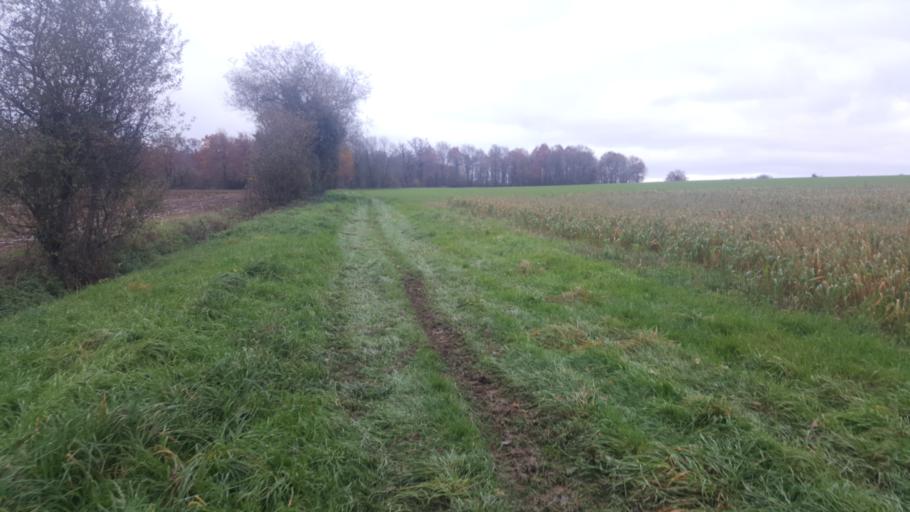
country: FR
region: Poitou-Charentes
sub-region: Departement des Deux-Sevres
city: Melle
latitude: 46.2349
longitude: -0.1172
